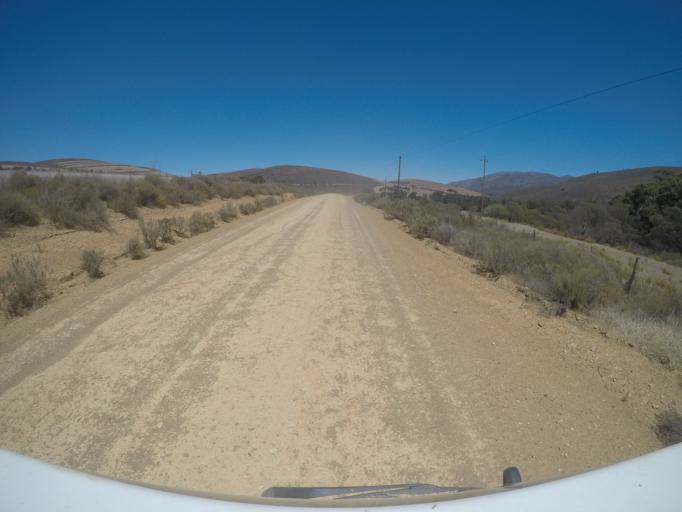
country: ZA
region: Western Cape
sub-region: Overberg District Municipality
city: Caledon
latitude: -34.1412
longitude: 19.2476
